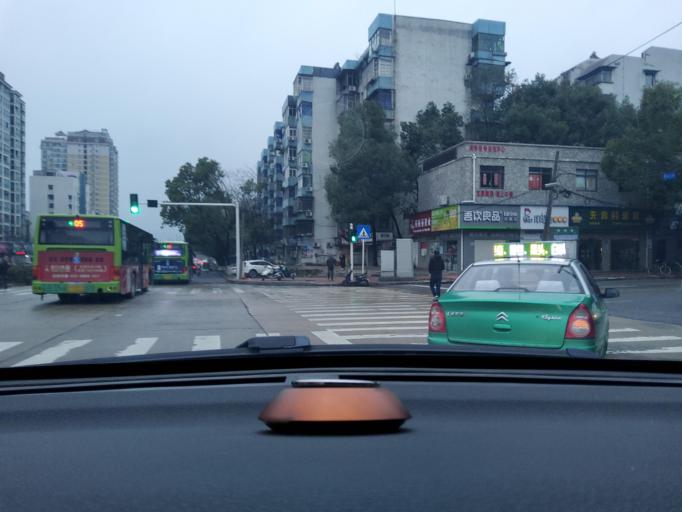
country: CN
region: Hubei
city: Tuanchengshan
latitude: 30.1931
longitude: 115.0274
